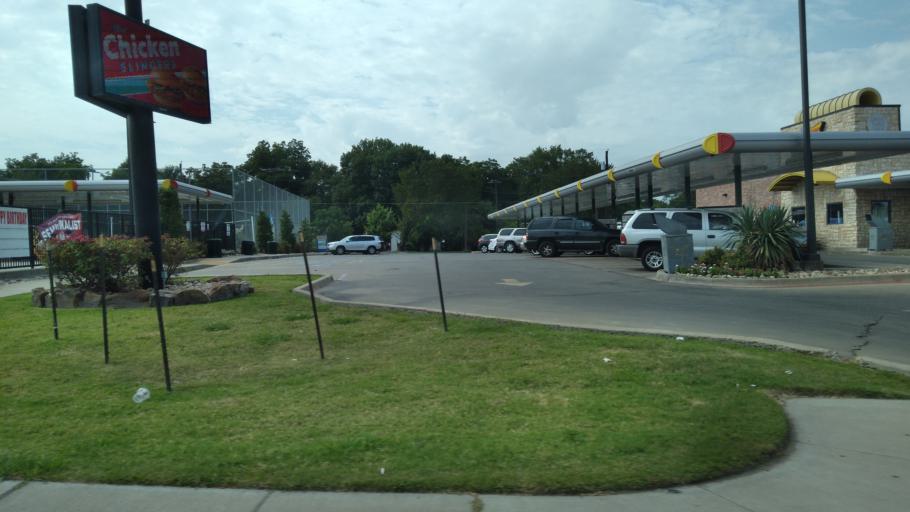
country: US
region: Texas
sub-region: Navarro County
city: Corsicana
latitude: 32.0833
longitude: -96.4807
